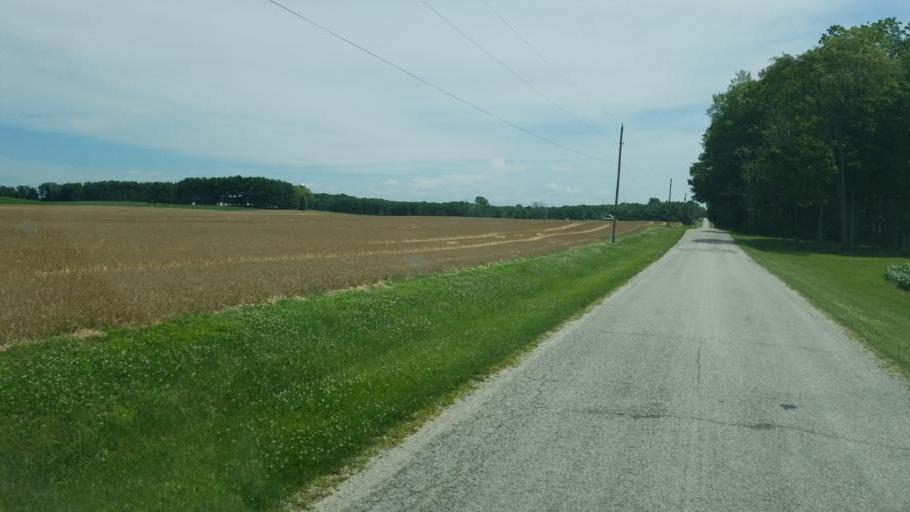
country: US
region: Ohio
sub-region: Crawford County
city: Bucyrus
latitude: 40.8710
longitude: -82.8908
